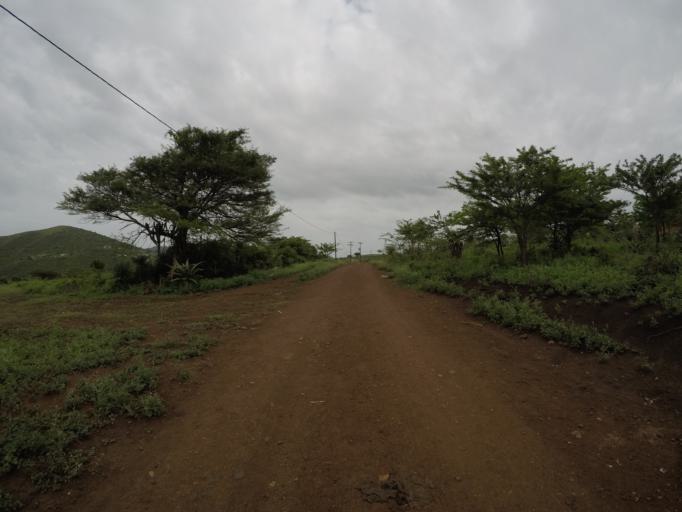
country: ZA
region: KwaZulu-Natal
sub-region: uThungulu District Municipality
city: Empangeni
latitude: -28.6409
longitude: 31.9063
